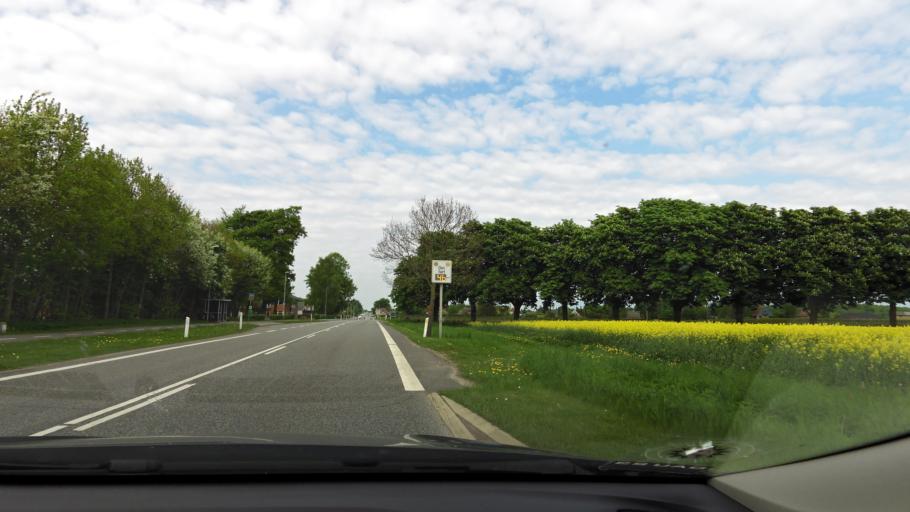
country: DK
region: South Denmark
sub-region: Nyborg Kommune
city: Ullerslev
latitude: 55.2789
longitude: 10.6861
